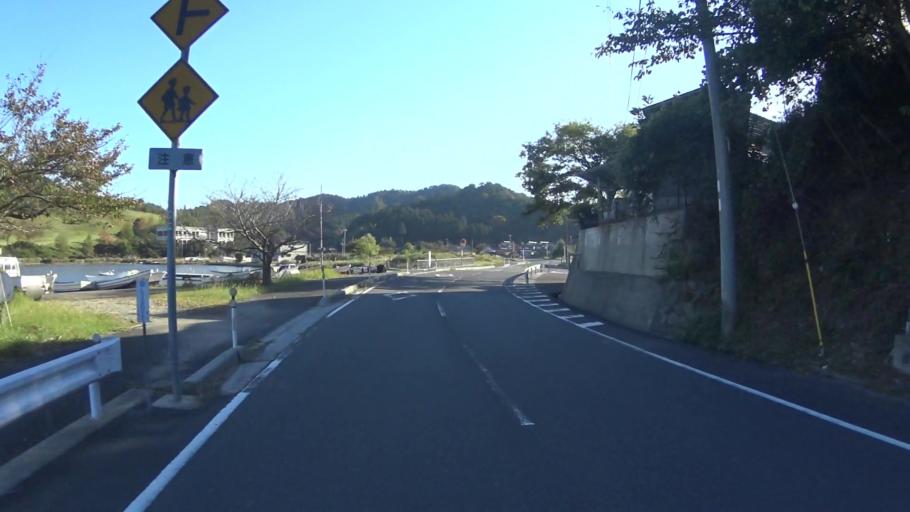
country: JP
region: Hyogo
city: Toyooka
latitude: 35.6297
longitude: 134.8877
